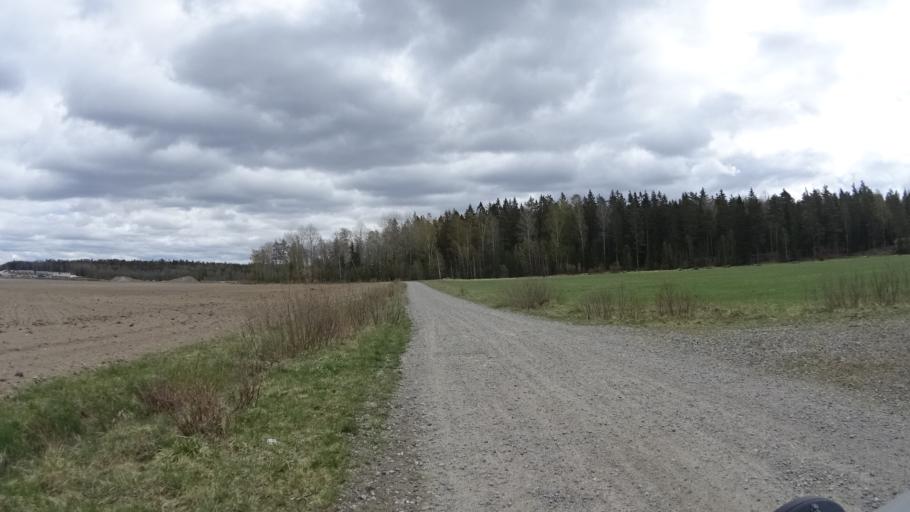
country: SE
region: Stockholm
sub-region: Botkyrka Kommun
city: Tullinge
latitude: 59.1760
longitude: 17.9006
